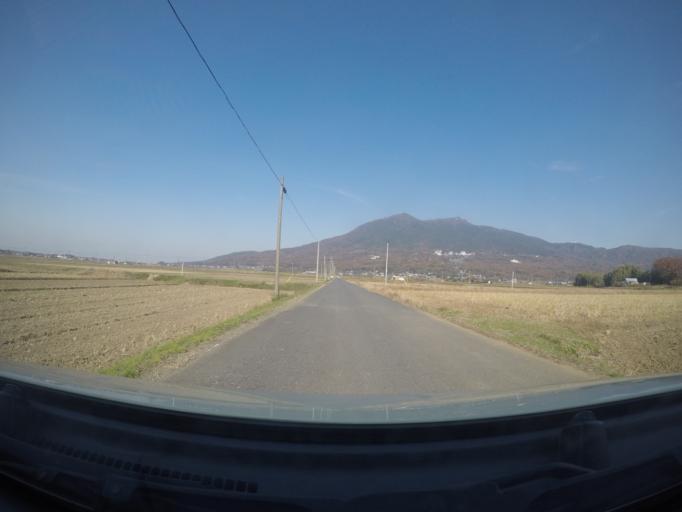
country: JP
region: Ibaraki
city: Tsukuba
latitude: 36.1923
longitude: 140.0895
